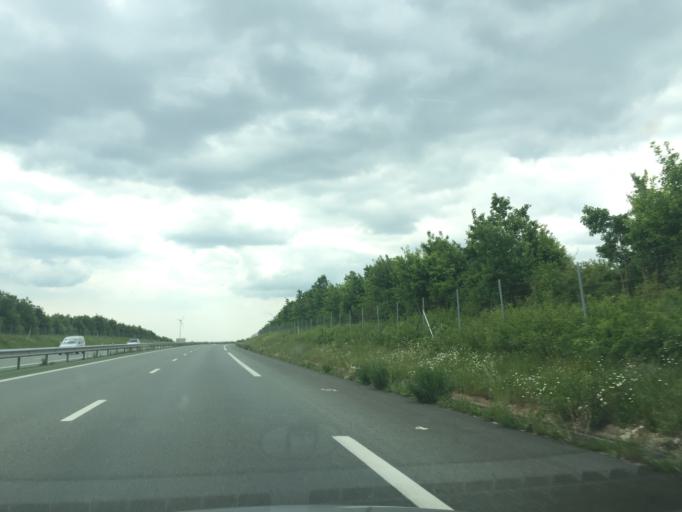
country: FR
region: Pays de la Loire
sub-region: Departement de la Vendee
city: Benet
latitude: 46.4057
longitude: -0.5851
